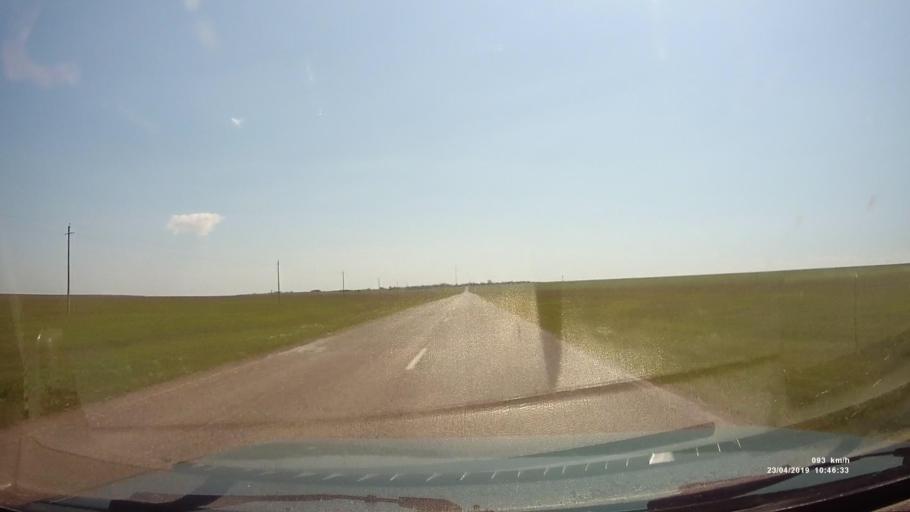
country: RU
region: Kalmykiya
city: Yashalta
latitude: 46.4421
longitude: 42.6930
